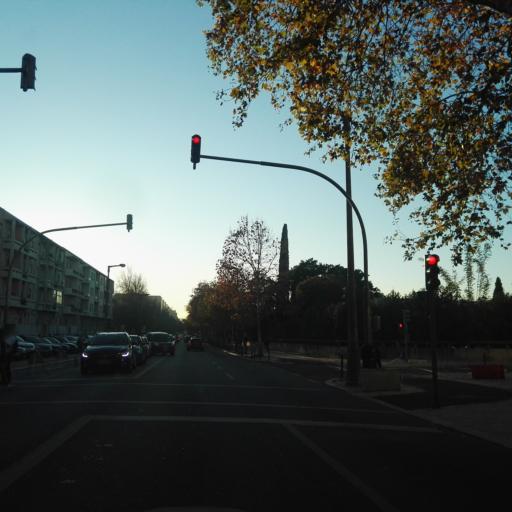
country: PT
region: Lisbon
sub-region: Loures
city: Moscavide
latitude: 38.7592
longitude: -9.1385
